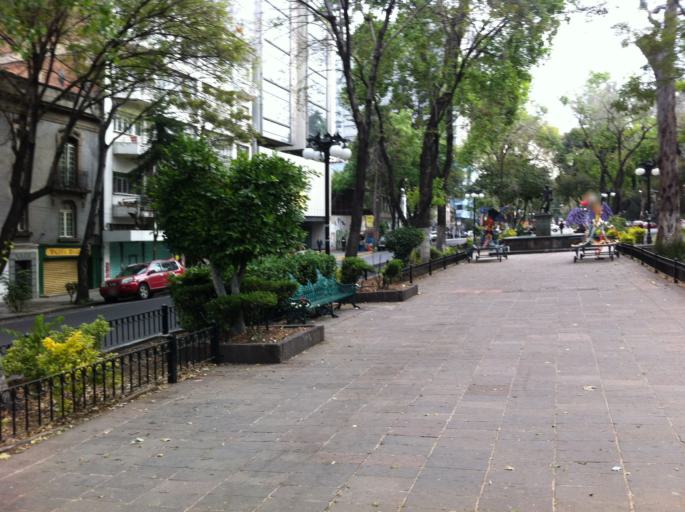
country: MX
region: Mexico City
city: Benito Juarez
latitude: 19.4178
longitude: -99.1622
